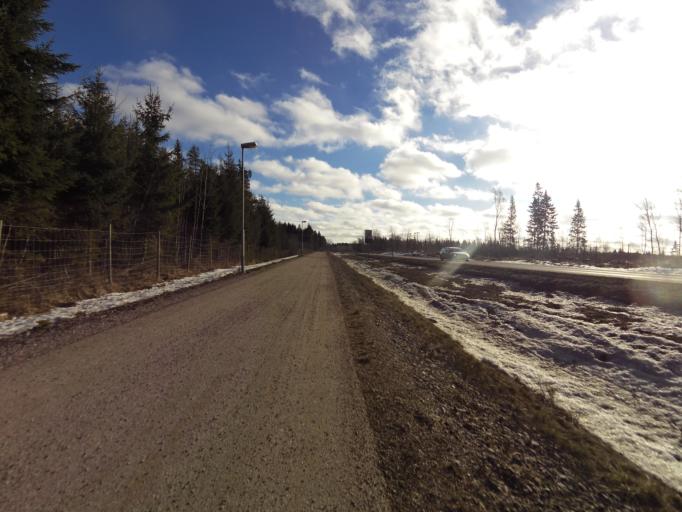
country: SE
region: Gaevleborg
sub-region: Gavle Kommun
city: Gavle
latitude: 60.6477
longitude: 17.2512
